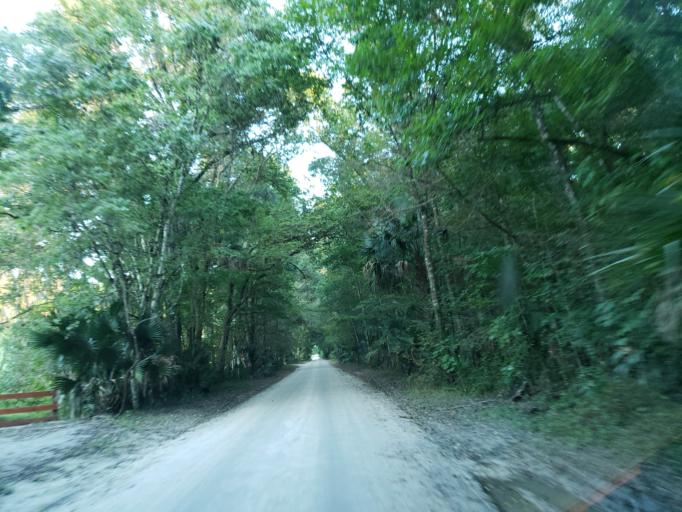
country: US
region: Florida
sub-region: Alachua County
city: Gainesville
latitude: 29.4842
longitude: -82.2722
